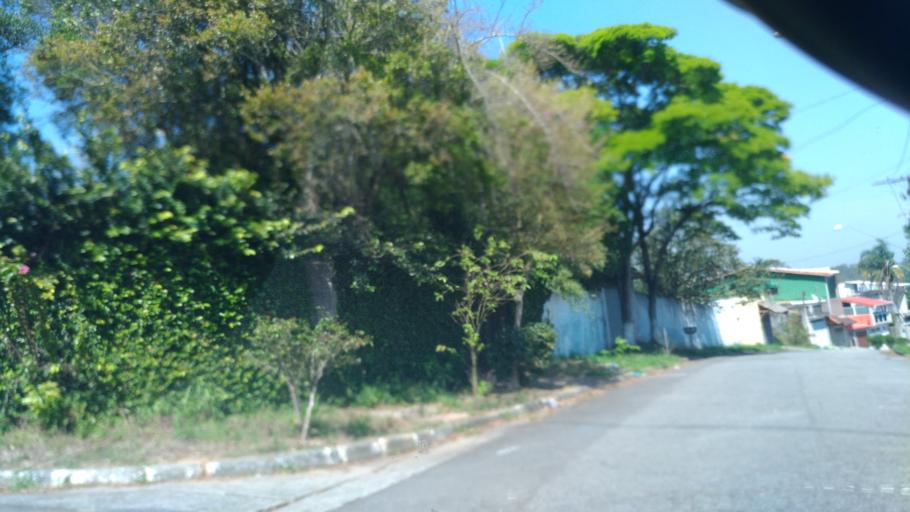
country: BR
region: Sao Paulo
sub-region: Sao Bernardo Do Campo
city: Sao Bernardo do Campo
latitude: -23.7762
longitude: -46.5175
